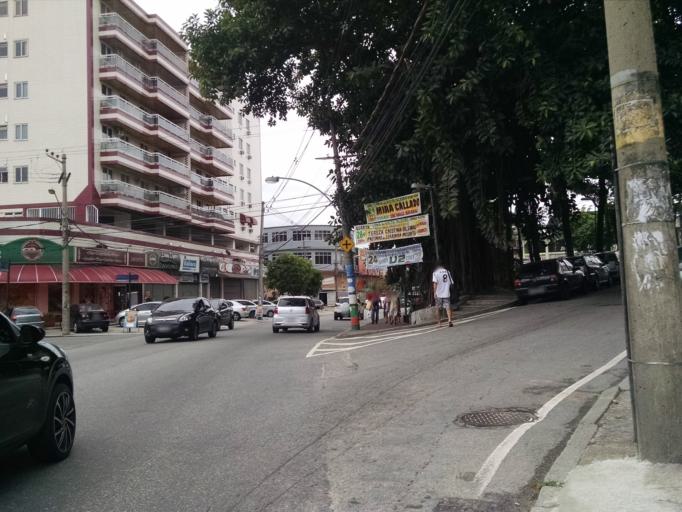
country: BR
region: Rio de Janeiro
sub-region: Duque De Caxias
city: Duque de Caxias
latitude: -22.8370
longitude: -43.3173
